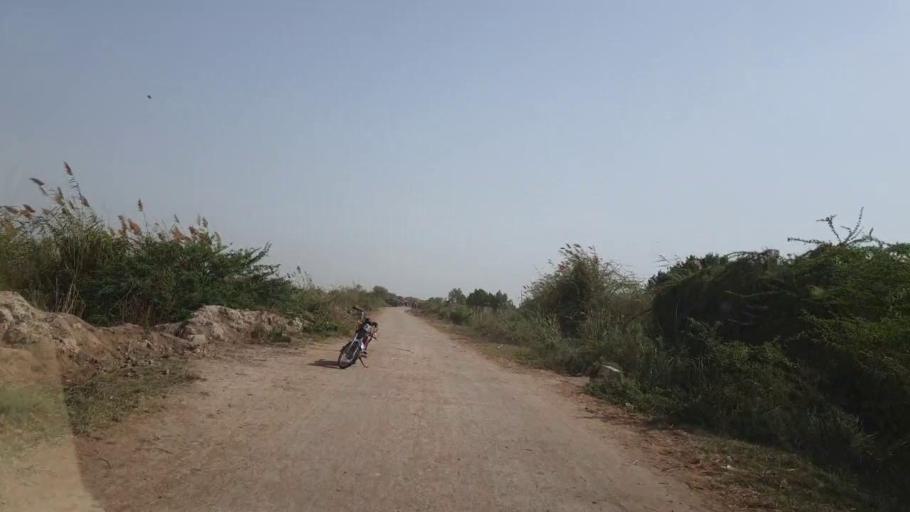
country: PK
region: Sindh
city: Rajo Khanani
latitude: 25.0523
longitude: 68.8413
